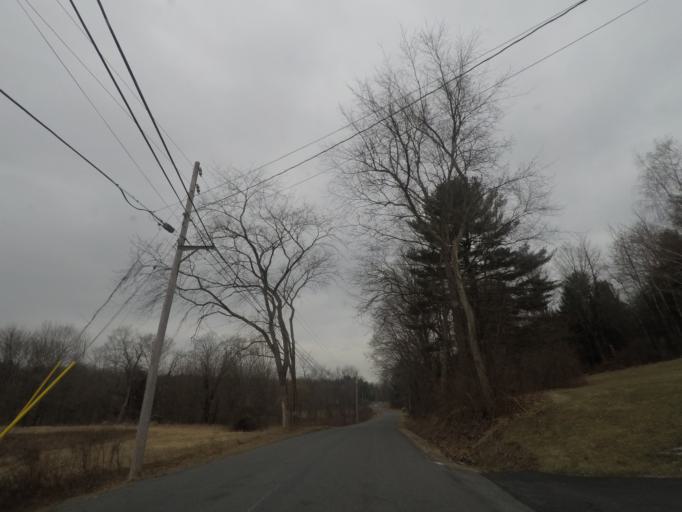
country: US
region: New York
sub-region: Rensselaer County
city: East Greenbush
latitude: 42.5633
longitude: -73.6567
